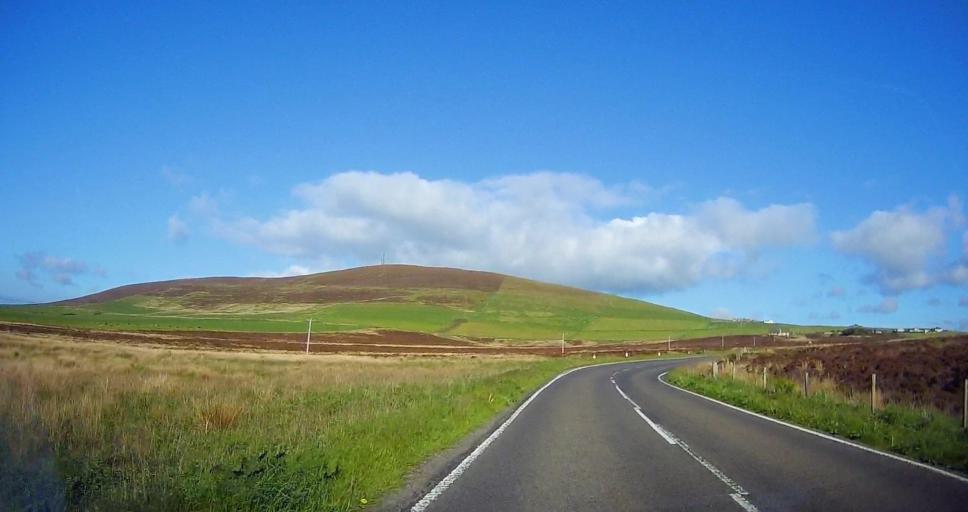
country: GB
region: Scotland
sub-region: Orkney Islands
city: Orkney
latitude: 58.9878
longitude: -3.0519
